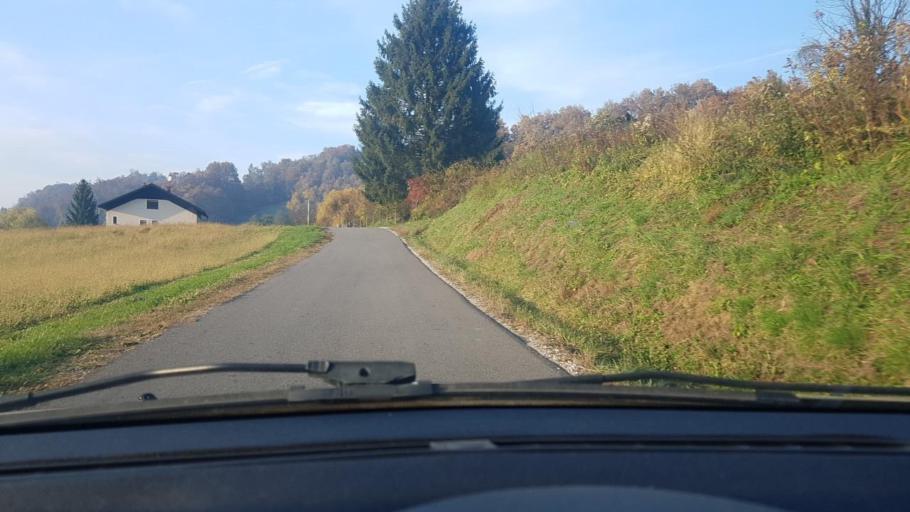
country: SI
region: Podcetrtek
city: Podcetrtek
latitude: 46.1552
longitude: 15.6153
